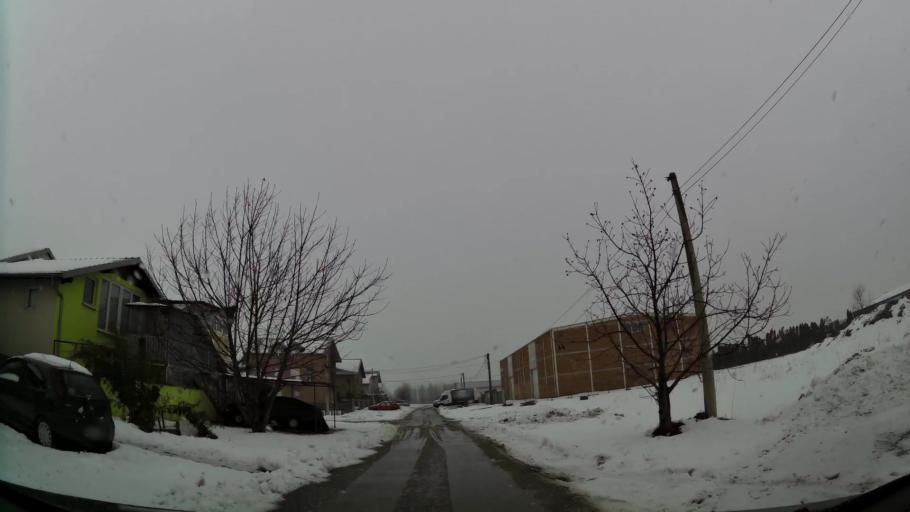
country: RS
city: Novi Banovci
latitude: 44.8792
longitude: 20.3178
